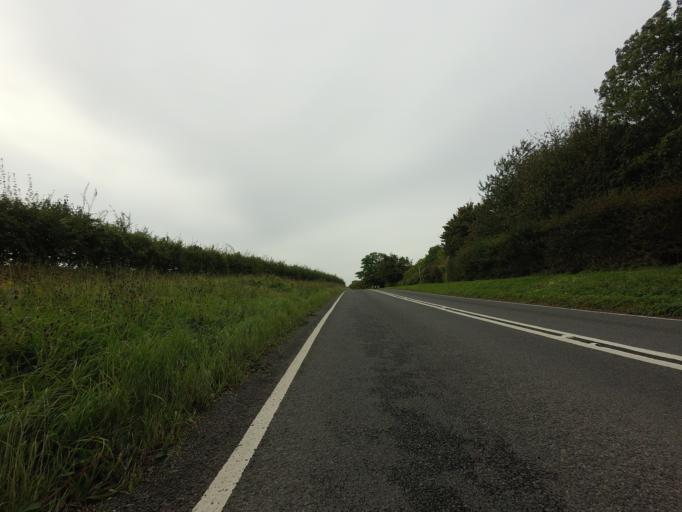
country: GB
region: England
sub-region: Hertfordshire
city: Reed
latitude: 52.0194
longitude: 0.0304
